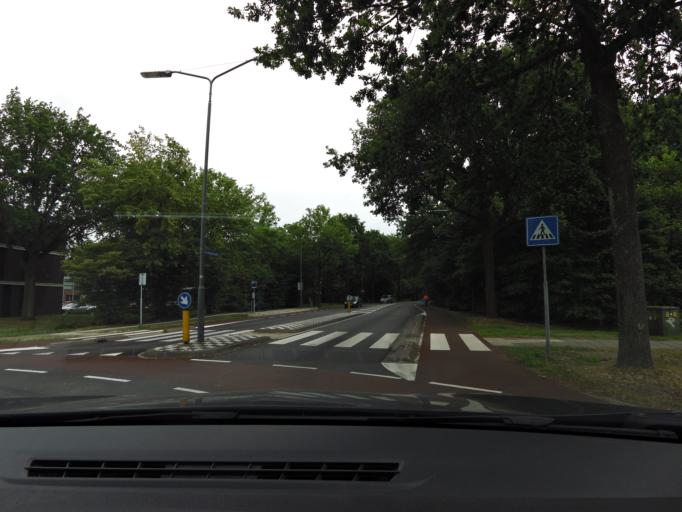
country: NL
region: North Brabant
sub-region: Gemeente Vught
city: Vught
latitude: 51.6459
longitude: 5.2958
